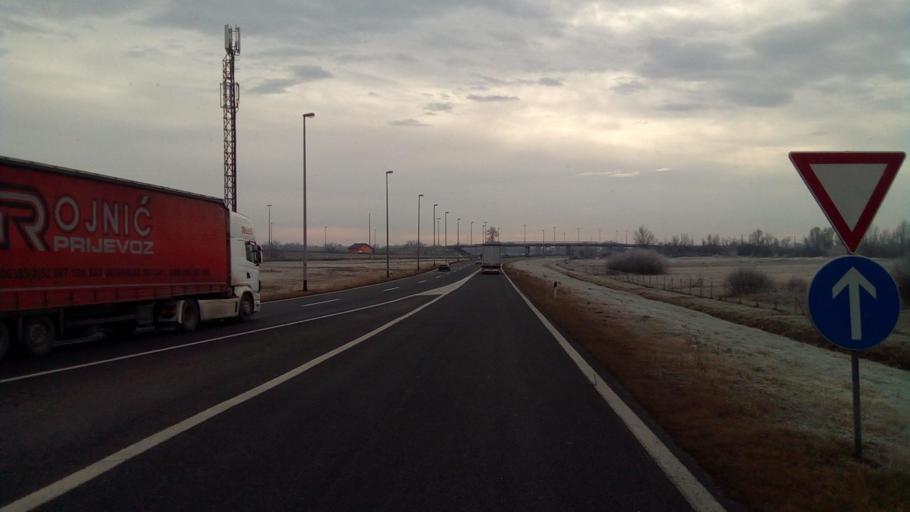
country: HR
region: Grad Zagreb
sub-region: Sesvete
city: Sesvete
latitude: 45.7964
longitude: 16.1293
